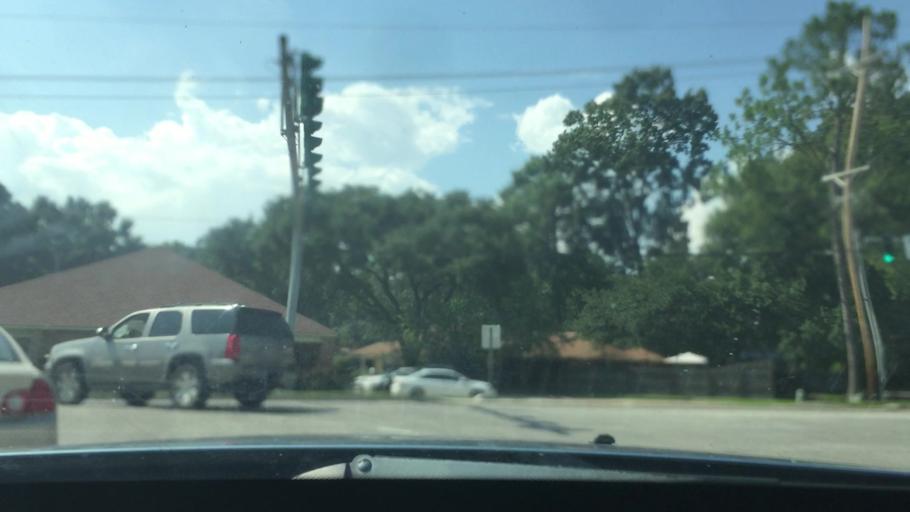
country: US
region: Louisiana
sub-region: East Baton Rouge Parish
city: Monticello
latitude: 30.4516
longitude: -91.0246
